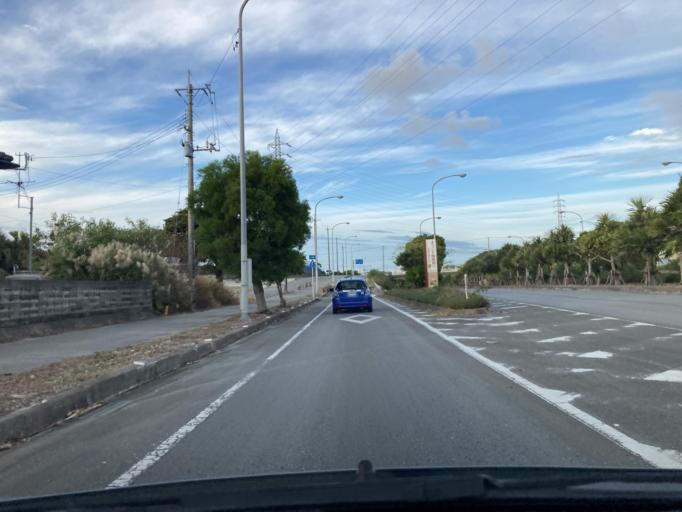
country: JP
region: Okinawa
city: Tomigusuku
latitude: 26.1714
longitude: 127.7266
